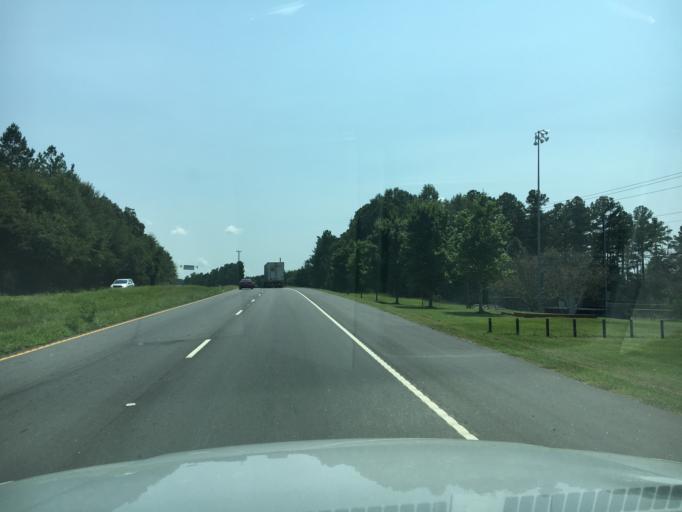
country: US
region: South Carolina
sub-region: Pickens County
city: Clemson
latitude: 34.6625
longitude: -82.8143
